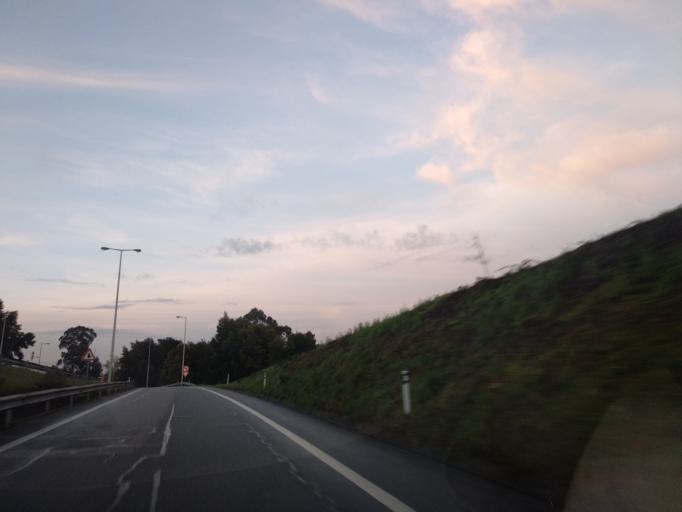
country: PT
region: Braga
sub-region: Vila Nova de Famalicao
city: Vila Nova de Famalicao
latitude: 41.3761
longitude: -8.5029
